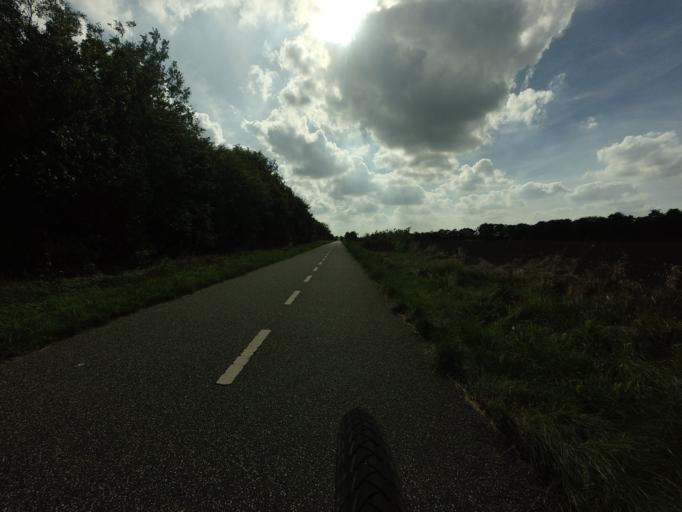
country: DK
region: Central Jutland
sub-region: Herning Kommune
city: Sunds
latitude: 56.1935
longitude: 9.0132
